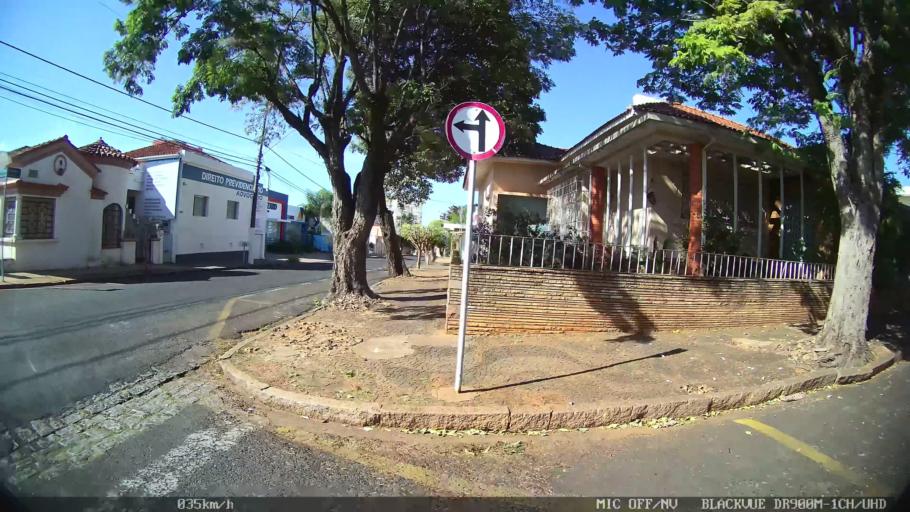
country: BR
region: Sao Paulo
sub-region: Olimpia
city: Olimpia
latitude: -20.7374
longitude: -48.9167
